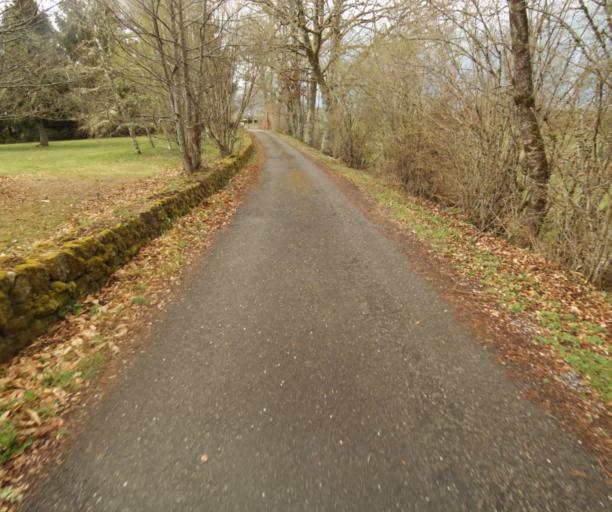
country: FR
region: Limousin
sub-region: Departement de la Correze
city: Egletons
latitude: 45.2569
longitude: 1.9920
